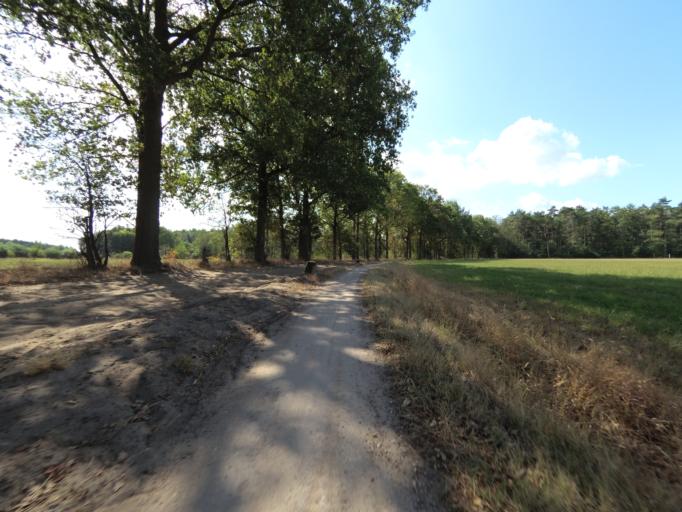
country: NL
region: Overijssel
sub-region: Gemeente Oldenzaal
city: Oldenzaal
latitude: 52.2805
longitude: 6.8798
